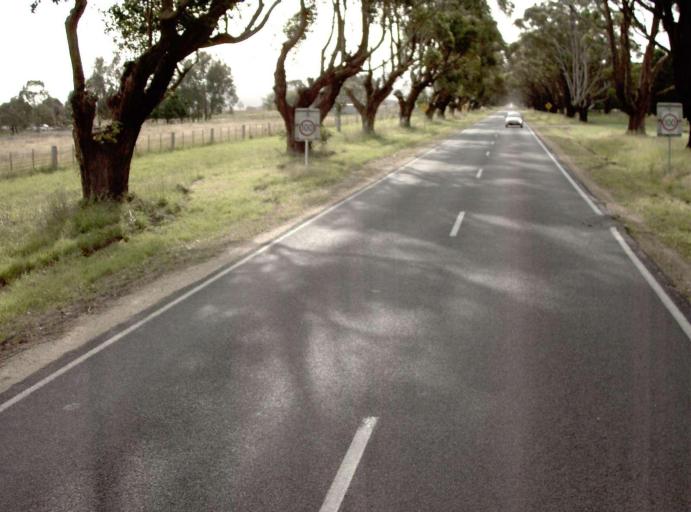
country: AU
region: Victoria
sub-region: Wellington
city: Heyfield
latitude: -38.0136
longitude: 146.6904
